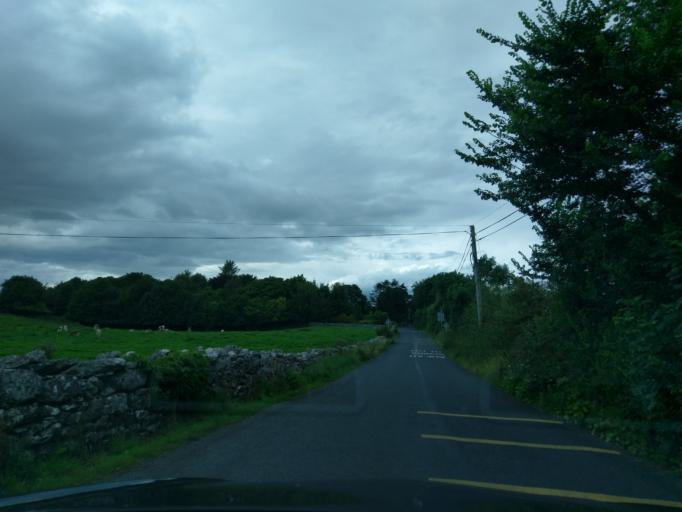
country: IE
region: Connaught
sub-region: County Galway
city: Athenry
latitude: 53.1994
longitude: -8.7112
